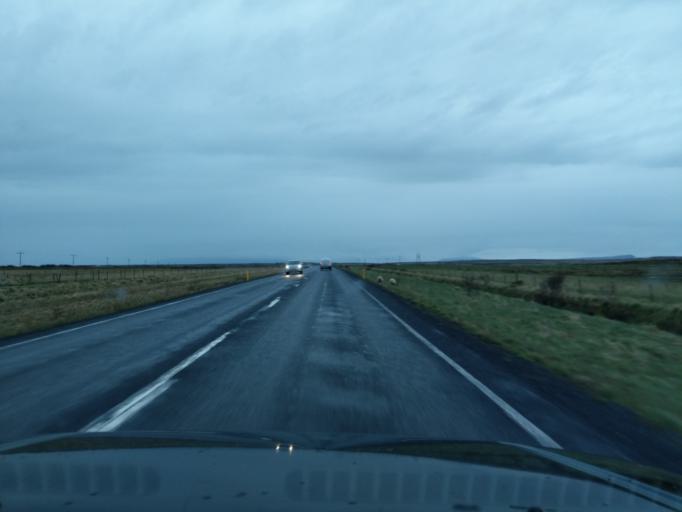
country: IS
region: South
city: Selfoss
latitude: 63.8874
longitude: -20.5280
